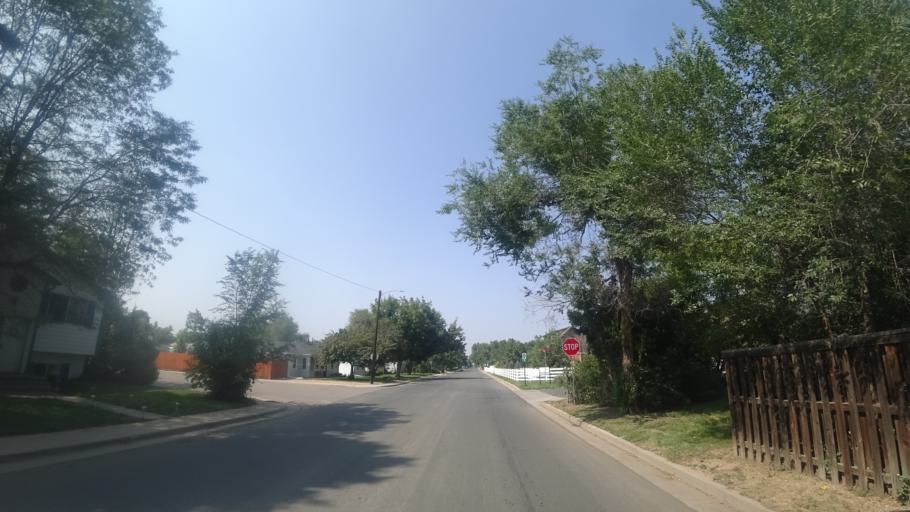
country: US
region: Colorado
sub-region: Arapahoe County
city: Englewood
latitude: 39.6329
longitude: -104.9785
